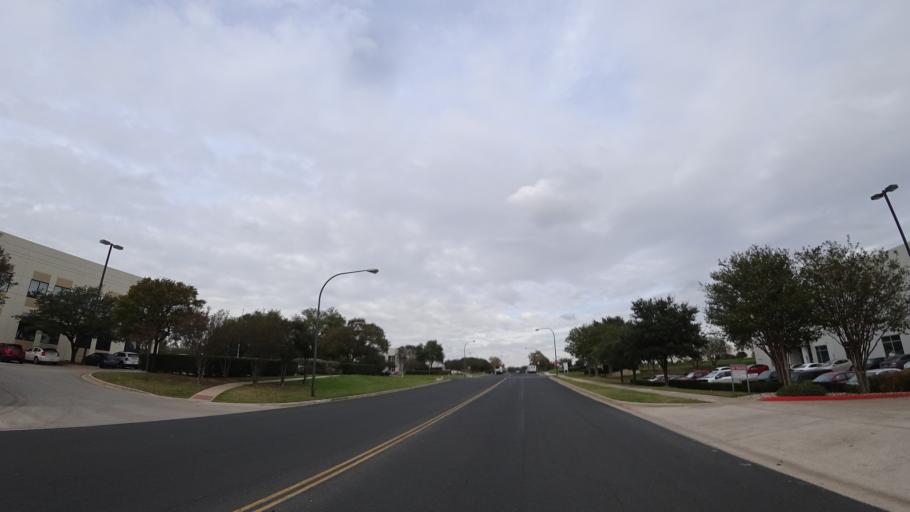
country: US
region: Texas
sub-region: Travis County
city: Wells Branch
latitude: 30.4532
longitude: -97.6768
